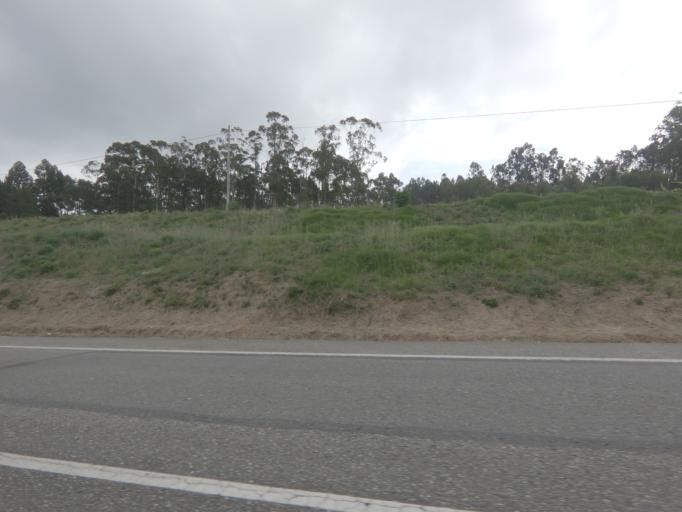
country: ES
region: Galicia
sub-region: Provincia de Pontevedra
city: O Rosal
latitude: 41.9328
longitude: -8.7946
